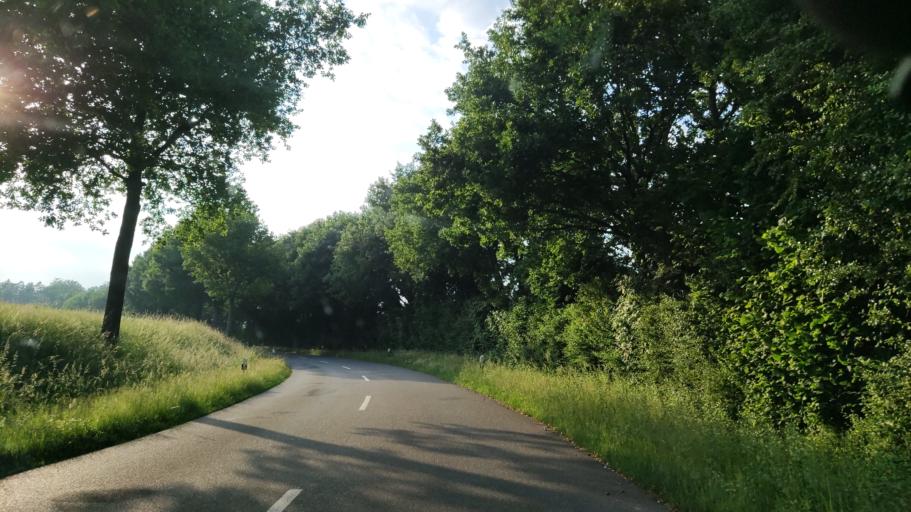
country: DE
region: Lower Saxony
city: Hanstedt Eins
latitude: 53.0312
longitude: 10.3541
